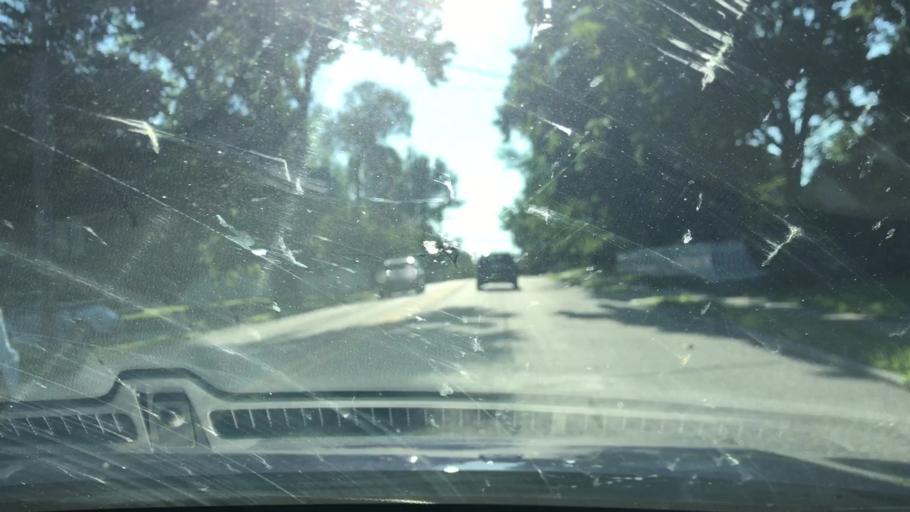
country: US
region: New Jersey
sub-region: Bergen County
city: Cresskill
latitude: 40.9413
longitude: -73.9752
